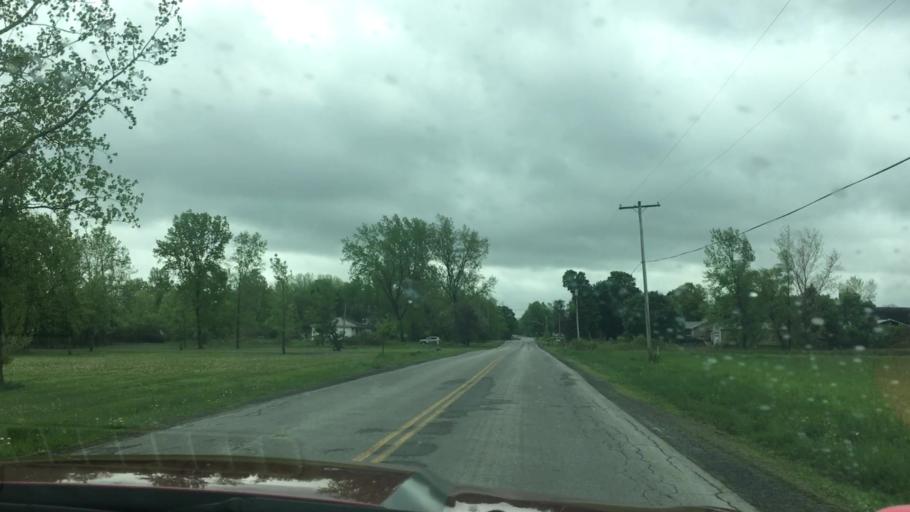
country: US
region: New York
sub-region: Genesee County
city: Batavia
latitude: 43.0774
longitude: -78.1396
